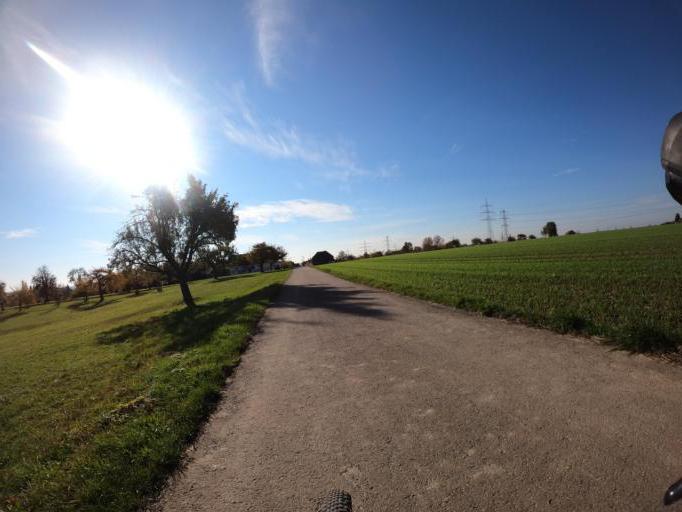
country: DE
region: Baden-Wuerttemberg
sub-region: Regierungsbezirk Stuttgart
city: Magstadt
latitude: 48.7295
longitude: 8.9576
